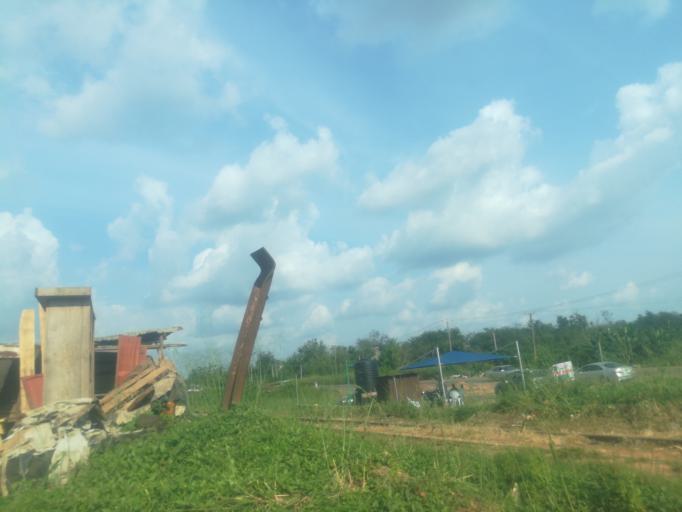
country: NG
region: Oyo
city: Ido
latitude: 7.3983
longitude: 3.7981
